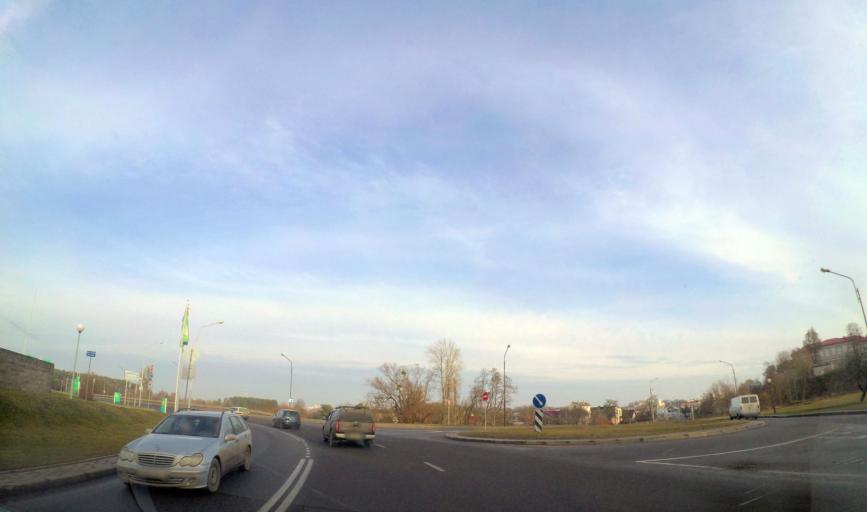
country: BY
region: Grodnenskaya
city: Hrodna
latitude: 53.6754
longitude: 23.8057
